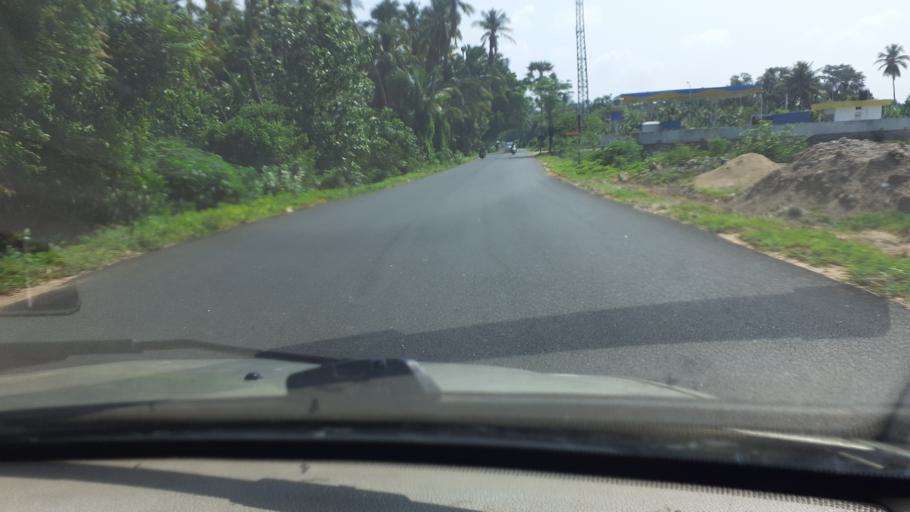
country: IN
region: Tamil Nadu
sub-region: Thoothukkudi
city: Srivaikuntam
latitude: 8.6343
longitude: 77.8937
